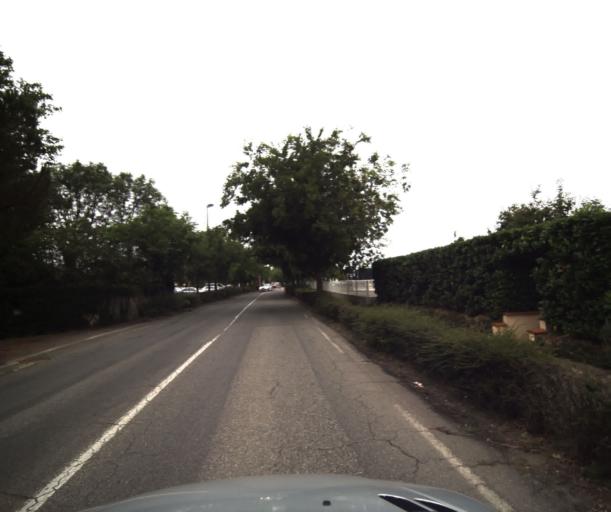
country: FR
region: Midi-Pyrenees
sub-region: Departement de la Haute-Garonne
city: Pinsaguel
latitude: 43.4997
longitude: 1.3924
